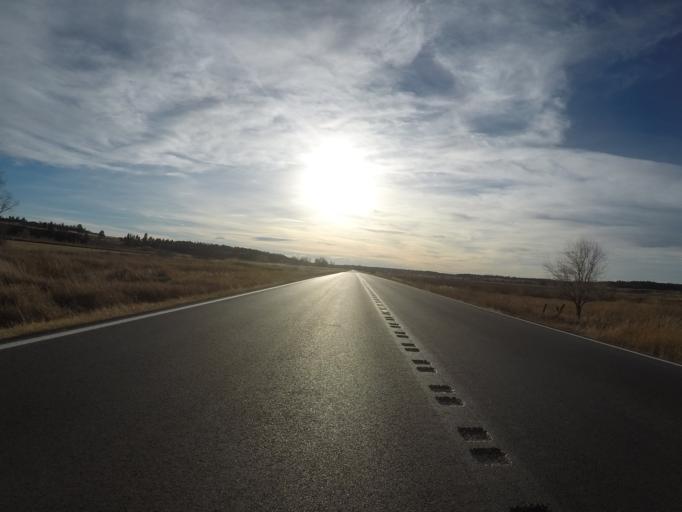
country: US
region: Montana
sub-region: Musselshell County
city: Roundup
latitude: 46.3544
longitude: -108.6712
